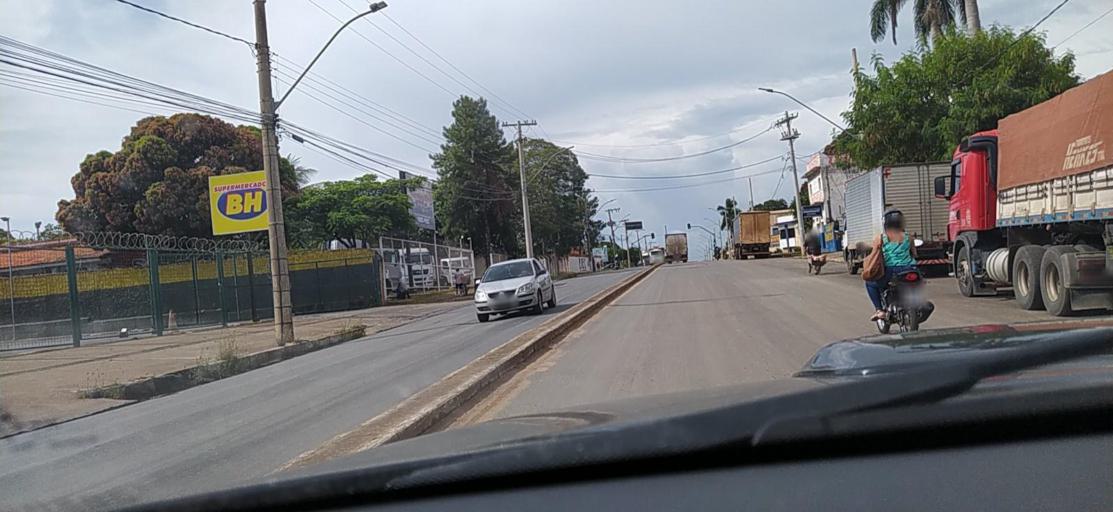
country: BR
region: Minas Gerais
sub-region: Montes Claros
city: Montes Claros
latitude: -16.7451
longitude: -43.8463
